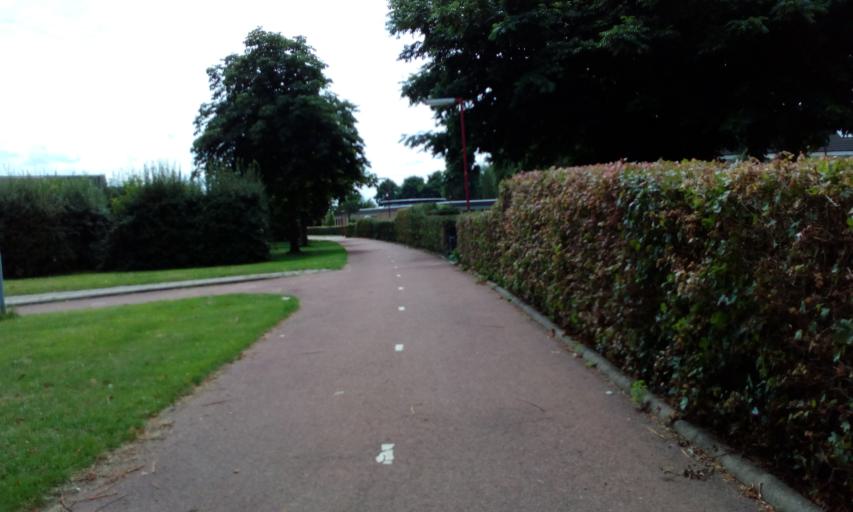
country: NL
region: South Holland
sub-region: Gemeente Zoetermeer
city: Zoetermeer
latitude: 52.0363
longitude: 4.4774
